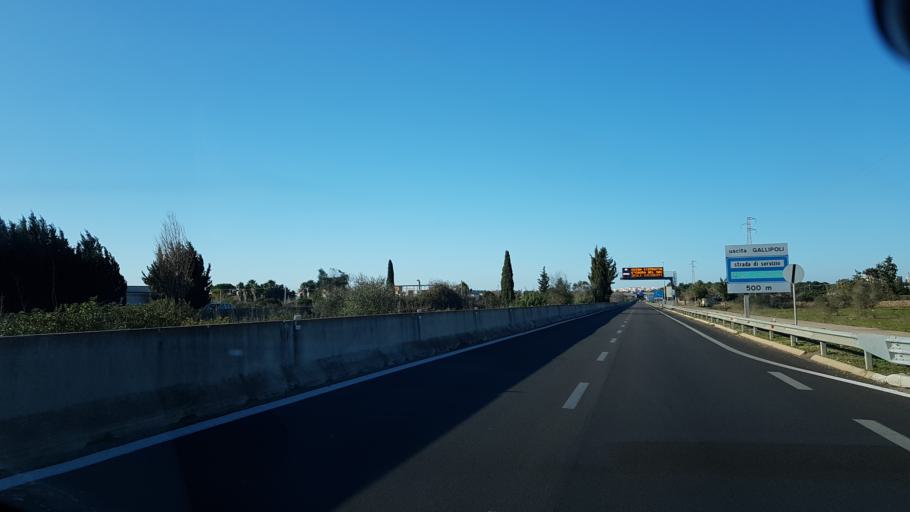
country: IT
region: Apulia
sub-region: Provincia di Lecce
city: Gallipoli
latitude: 40.0344
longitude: 18.0271
